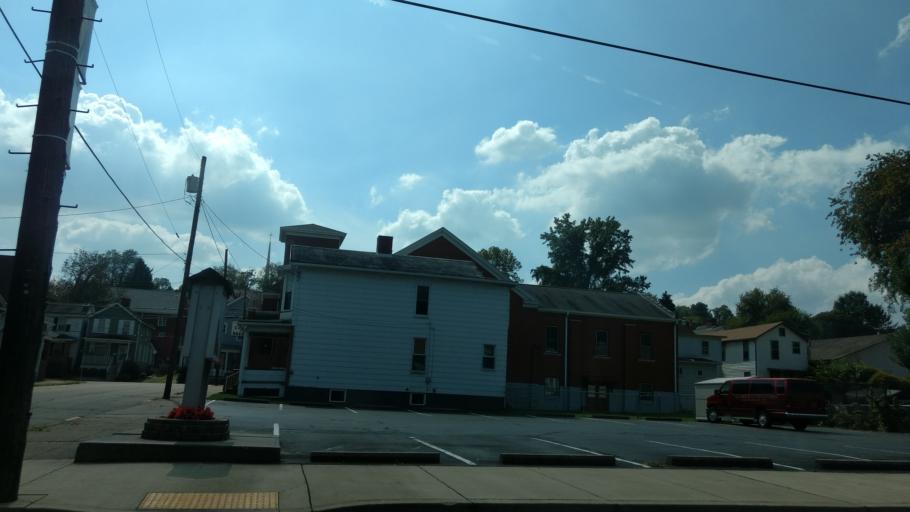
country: US
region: Pennsylvania
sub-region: Washington County
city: Monongahela
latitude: 40.2059
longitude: -79.9348
